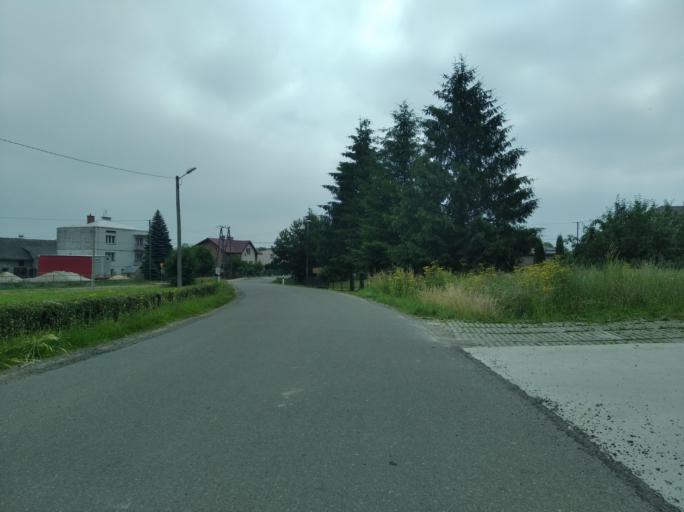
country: PL
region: Subcarpathian Voivodeship
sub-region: Powiat sanocki
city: Besko
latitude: 49.5928
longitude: 21.9383
